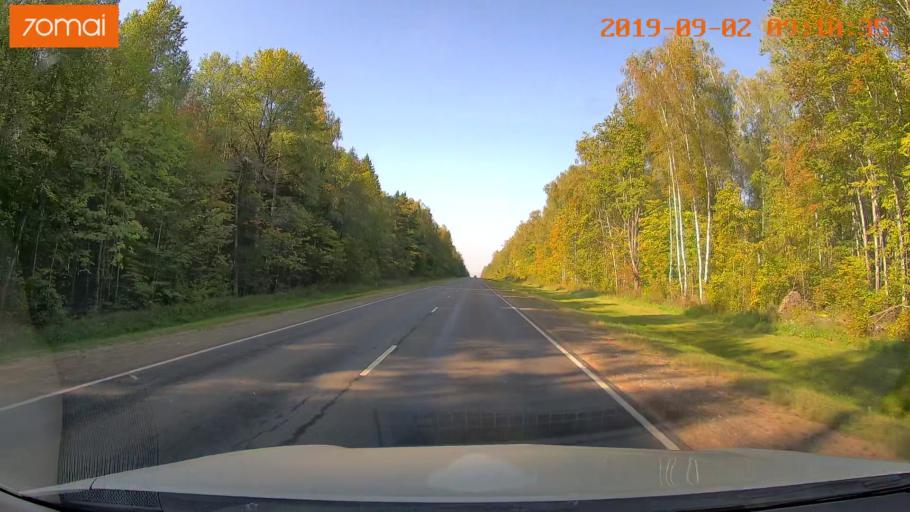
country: RU
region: Kaluga
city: Myatlevo
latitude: 54.8748
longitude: 35.5968
